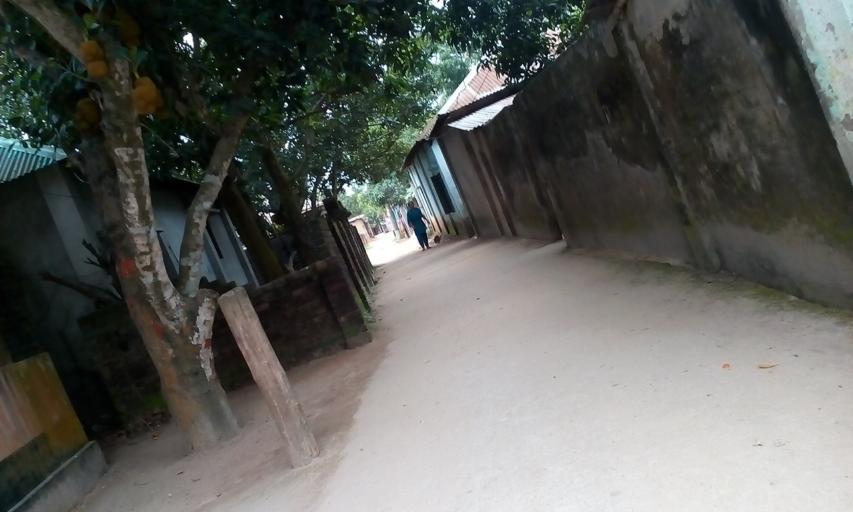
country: IN
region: West Bengal
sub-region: Dakshin Dinajpur
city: Balurghat
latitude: 25.3835
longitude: 88.9942
